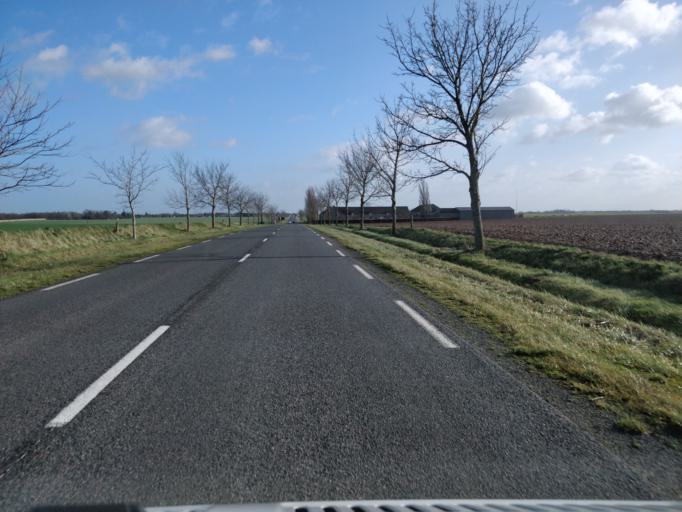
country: FR
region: Bourgogne
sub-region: Departement de l'Yonne
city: Cheroy
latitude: 48.2057
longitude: 2.9639
